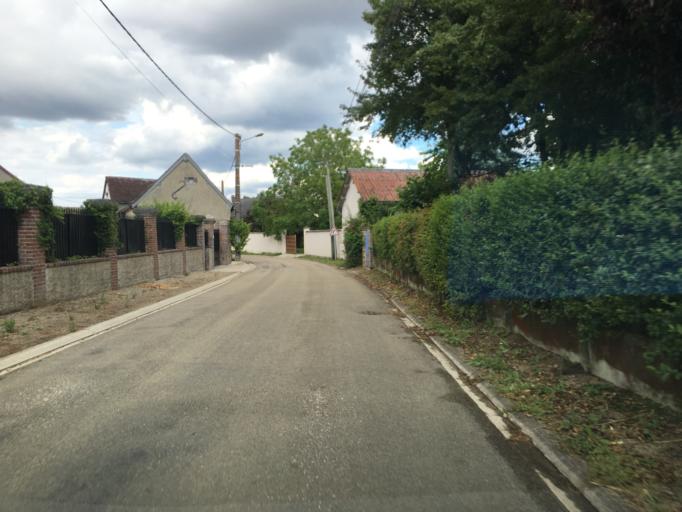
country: FR
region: Bourgogne
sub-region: Departement de l'Yonne
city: Aillant-sur-Tholon
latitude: 47.8237
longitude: 3.3948
